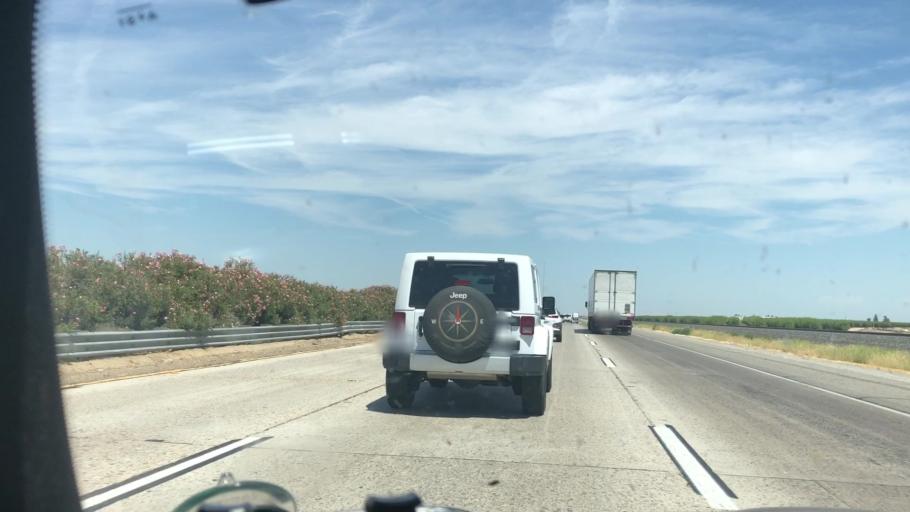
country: US
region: California
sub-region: Kern County
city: McFarland
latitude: 35.6151
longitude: -119.2122
